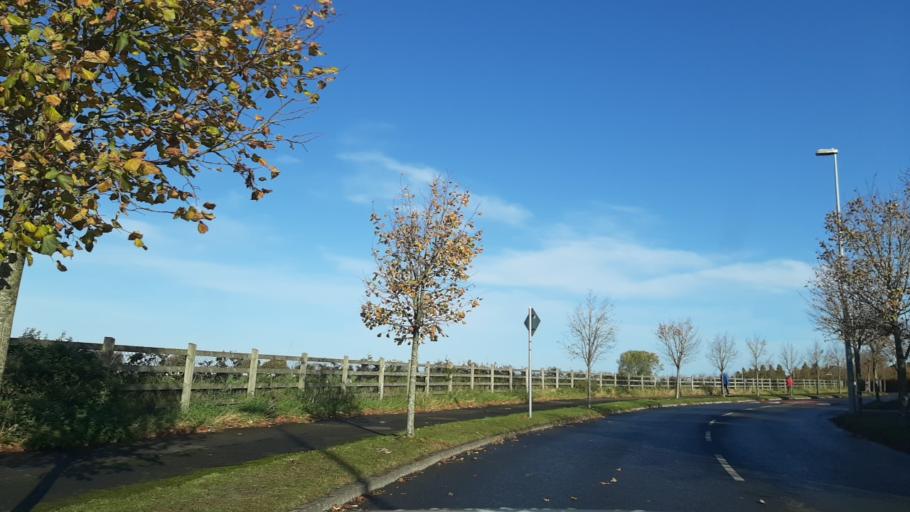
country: IE
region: Leinster
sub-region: Kildare
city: Rathangan
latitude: 53.2214
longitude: -7.0076
